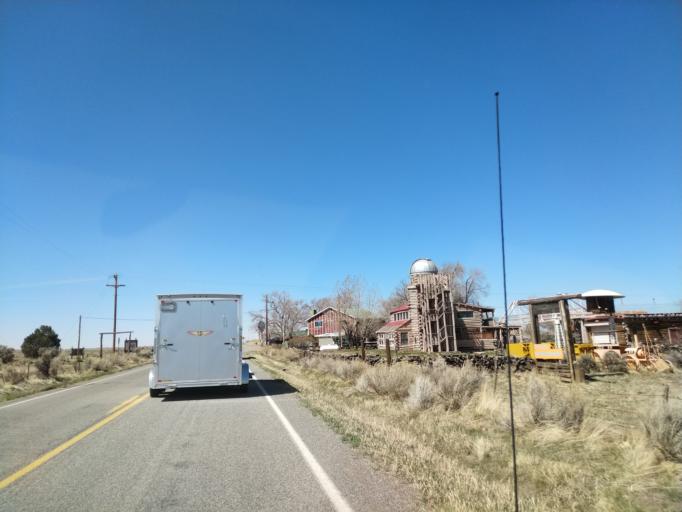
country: US
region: Colorado
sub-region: Mesa County
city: Redlands
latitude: 38.9938
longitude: -108.7396
